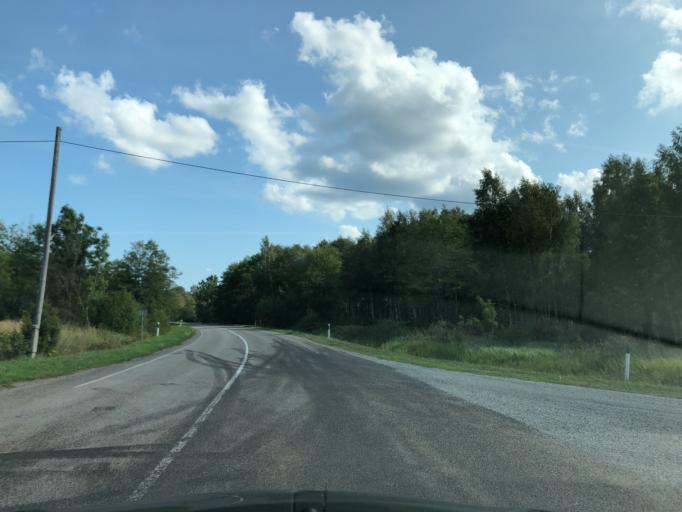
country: EE
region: Hiiumaa
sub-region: Kaerdla linn
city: Kardla
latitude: 58.7194
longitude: 22.5643
